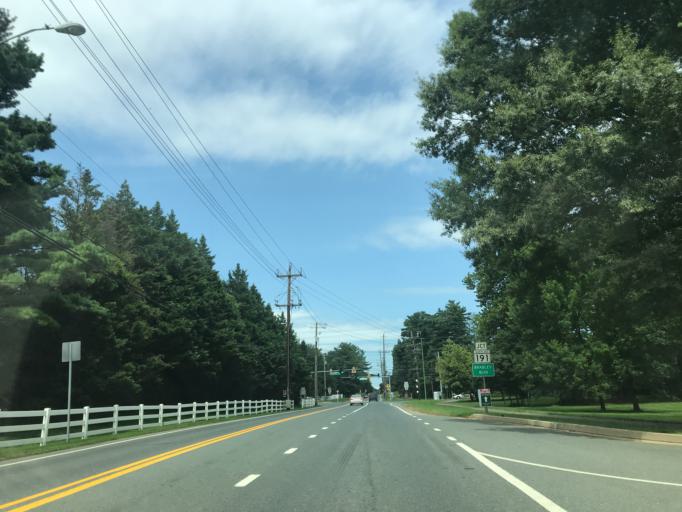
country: US
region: Maryland
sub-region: Montgomery County
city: Potomac
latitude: 39.0015
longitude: -77.1795
